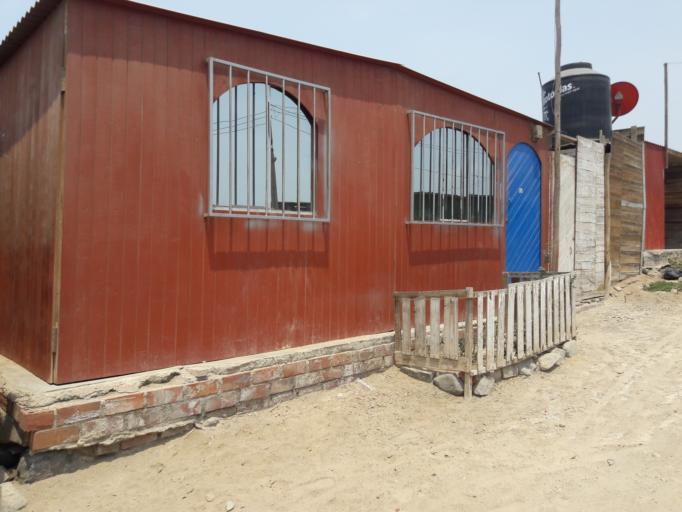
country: PE
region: Lima
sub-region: Lima
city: Santa Rosa
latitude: -11.7703
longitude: -77.1633
